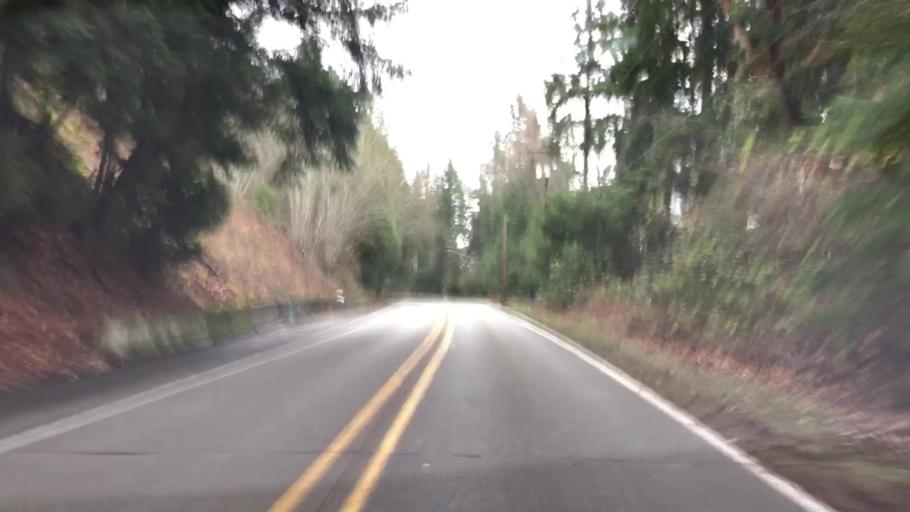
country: US
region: Washington
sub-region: King County
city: Sammamish
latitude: 47.6200
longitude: -122.0956
